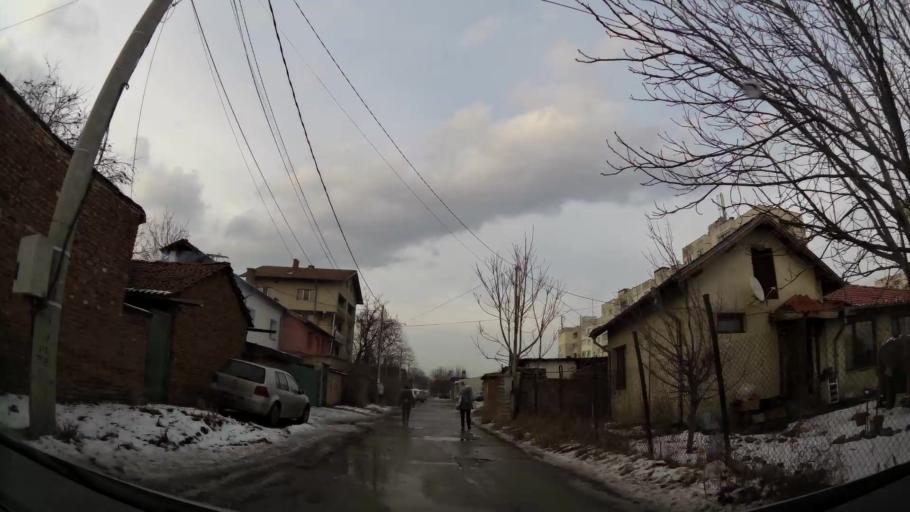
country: BG
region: Sofia-Capital
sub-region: Stolichna Obshtina
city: Sofia
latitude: 42.7214
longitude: 23.3481
